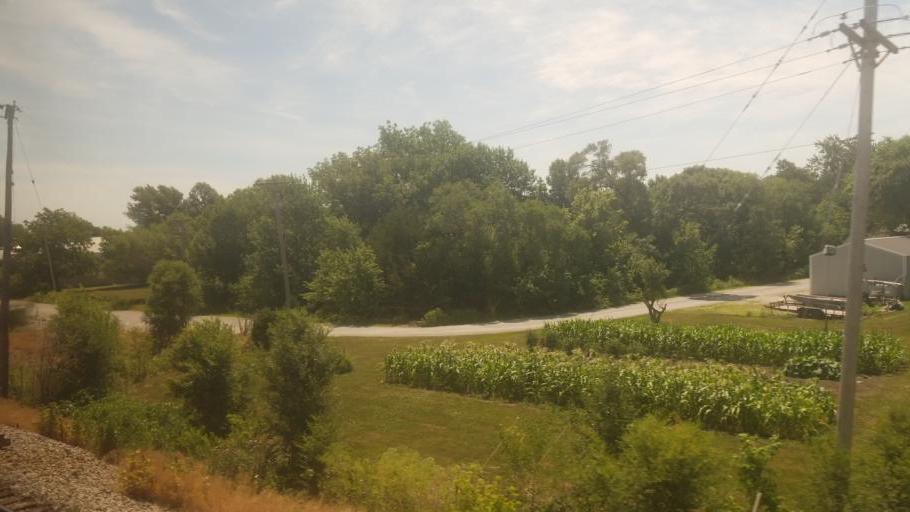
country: US
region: Missouri
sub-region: Carroll County
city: Carrollton
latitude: 39.3022
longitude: -93.6836
